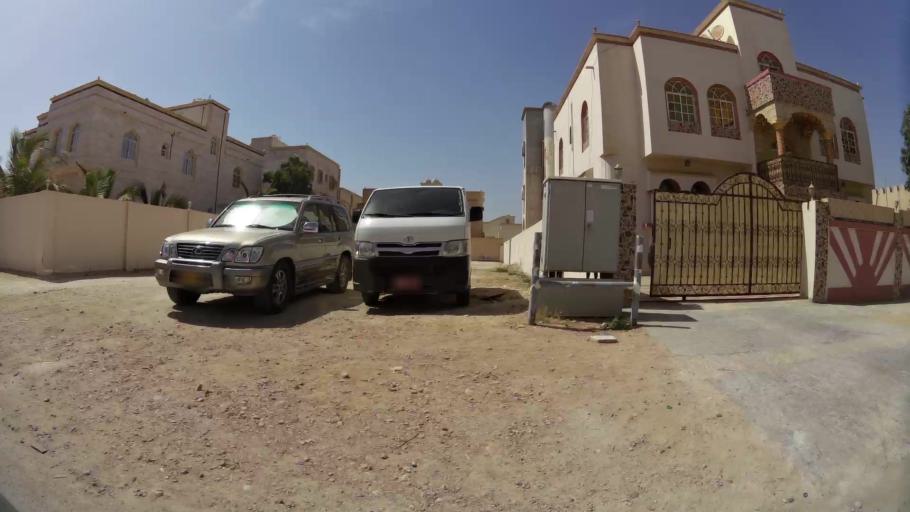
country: OM
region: Zufar
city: Salalah
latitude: 17.0399
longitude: 54.1592
